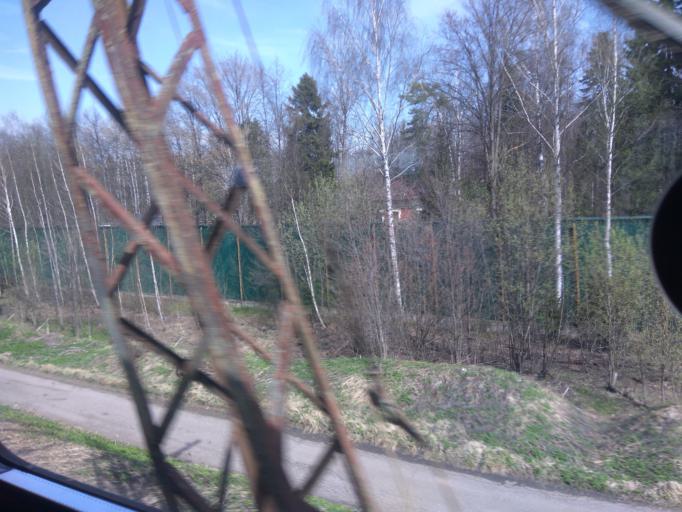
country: RU
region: Moskovskaya
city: Yermolino
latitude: 56.1368
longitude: 37.5118
